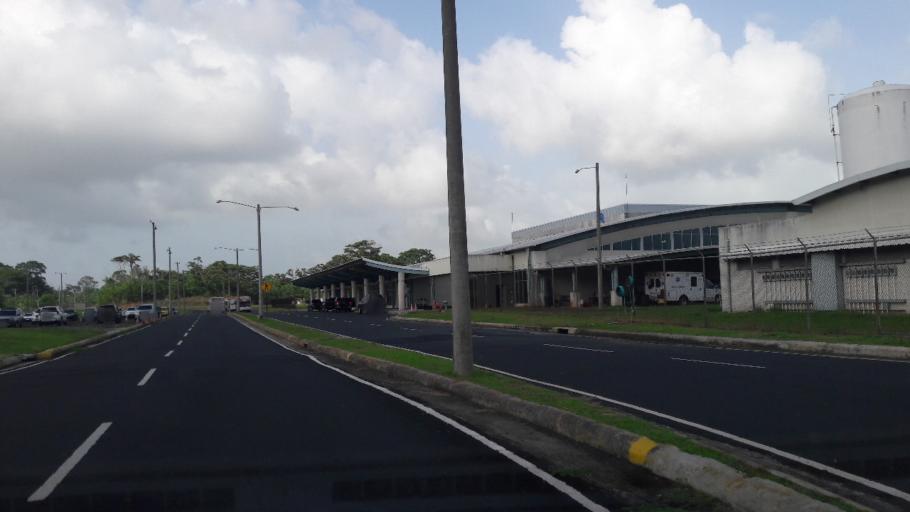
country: PA
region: Colon
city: Cativa
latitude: 9.3609
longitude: -79.8637
